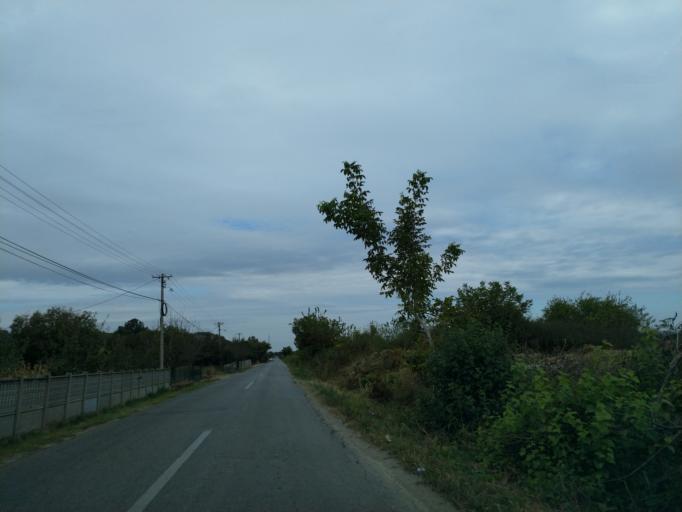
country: RS
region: Central Serbia
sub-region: Pomoravski Okrug
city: Cuprija
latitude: 43.9400
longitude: 21.3204
